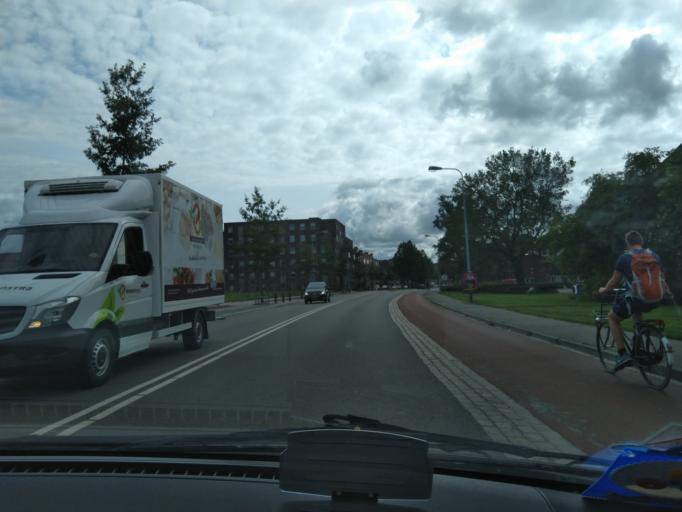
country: NL
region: Groningen
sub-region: Gemeente Groningen
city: Groningen
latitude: 53.2089
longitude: 6.5572
